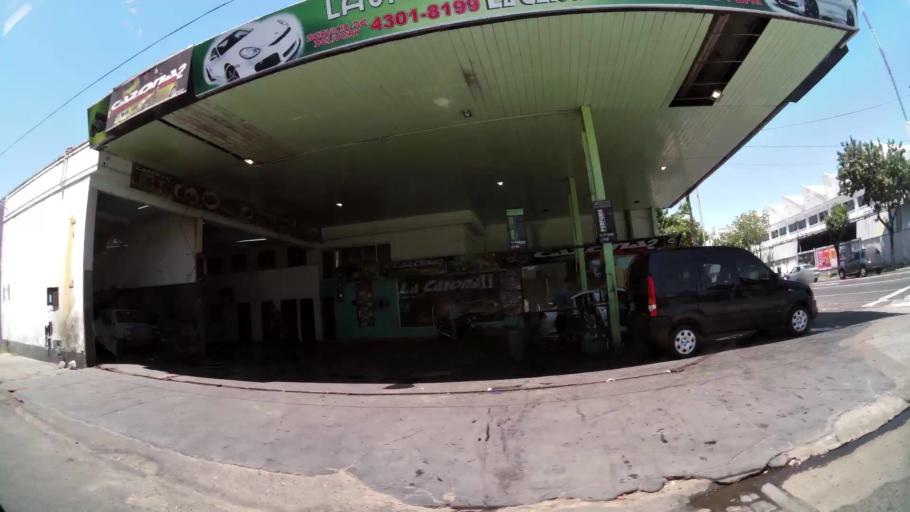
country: AR
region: Buenos Aires
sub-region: Partido de Avellaneda
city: Avellaneda
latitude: -34.6582
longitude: -58.3883
